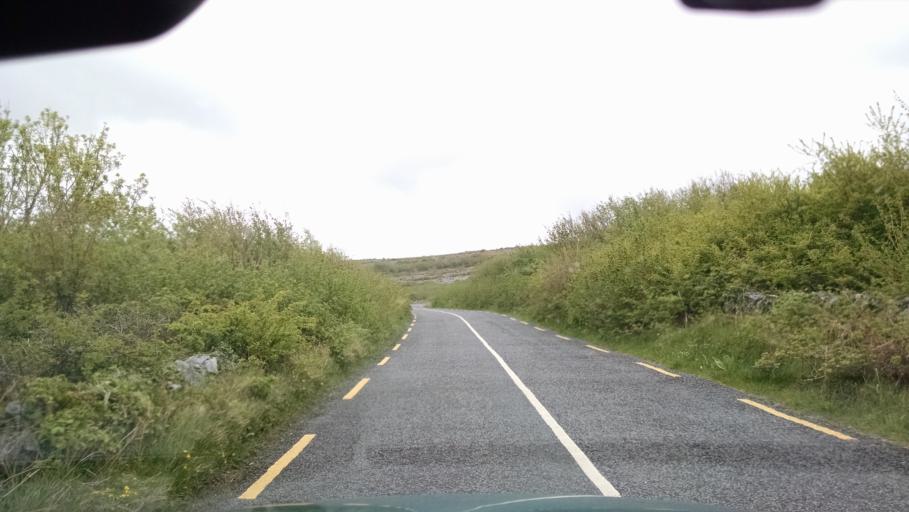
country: IE
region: Connaught
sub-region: County Galway
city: Bearna
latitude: 53.0852
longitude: -9.1635
